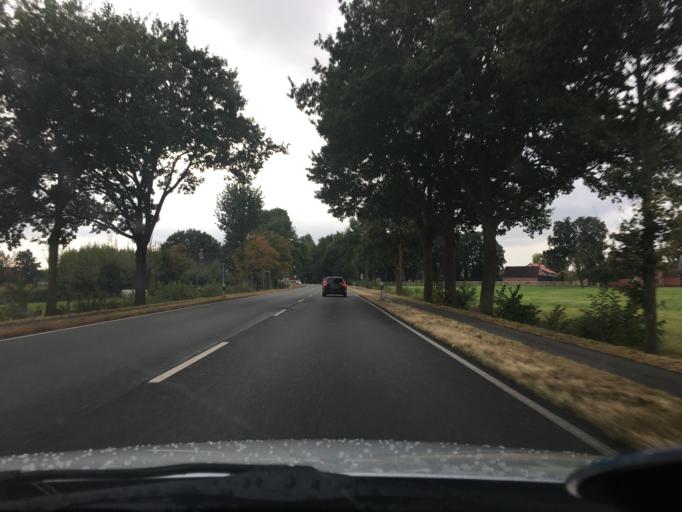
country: DE
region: Lower Saxony
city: Alfhausen
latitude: 52.4918
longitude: 7.9581
